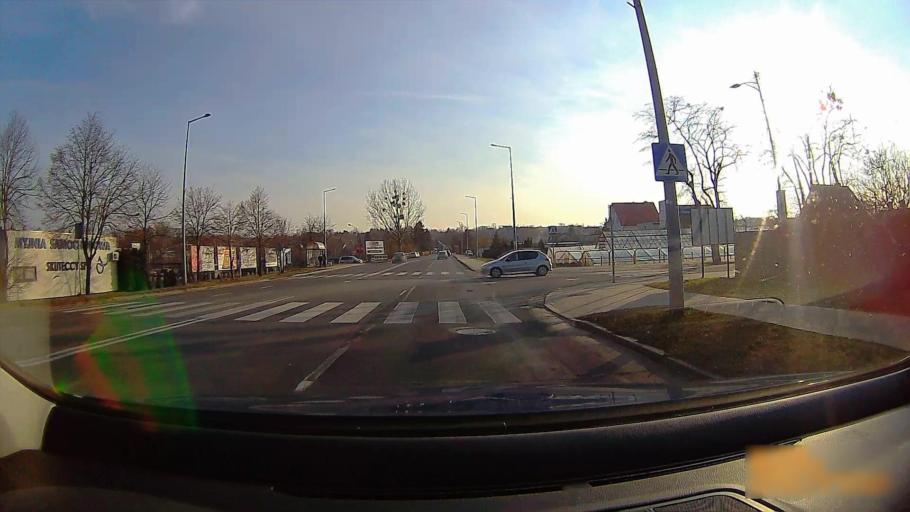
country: PL
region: Greater Poland Voivodeship
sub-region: Konin
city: Konin
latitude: 52.2069
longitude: 18.2627
